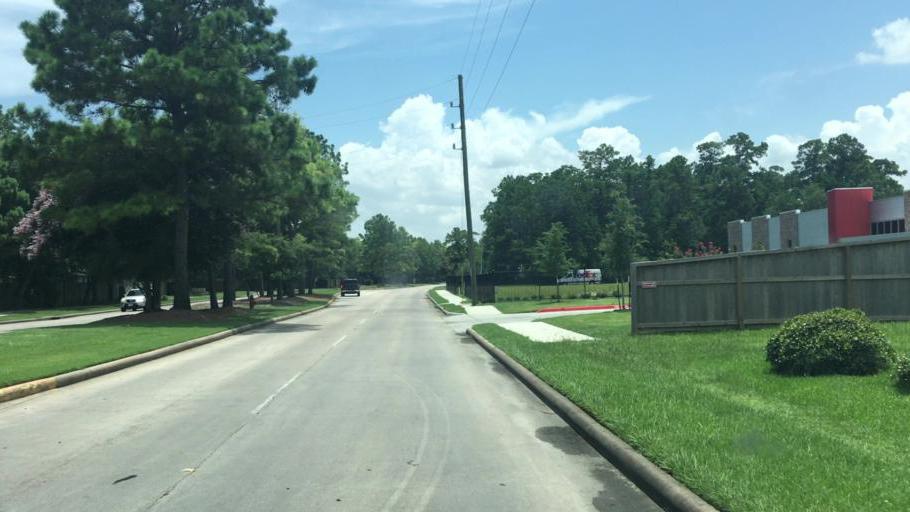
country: US
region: Texas
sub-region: Harris County
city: Atascocita
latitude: 29.9866
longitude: -95.1919
